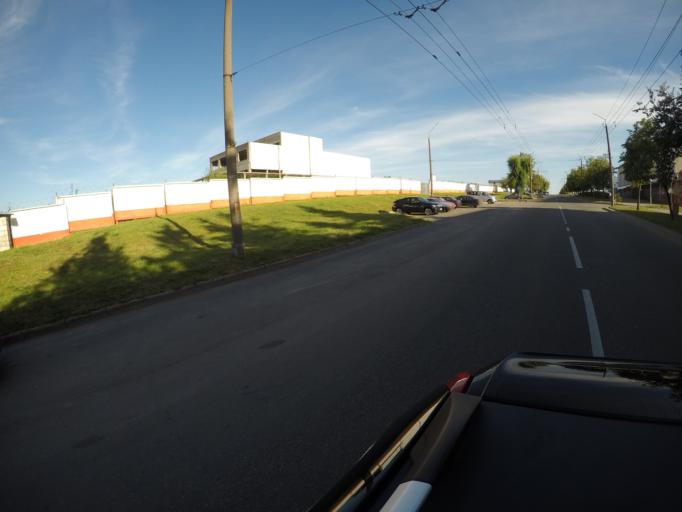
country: BY
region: Grodnenskaya
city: Hrodna
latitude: 53.7119
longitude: 23.8264
